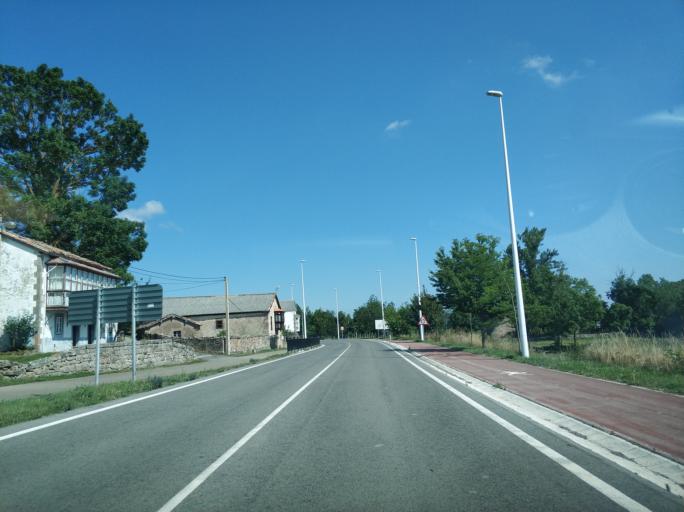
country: ES
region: Cantabria
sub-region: Provincia de Cantabria
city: Villaescusa
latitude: 43.0213
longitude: -4.2273
